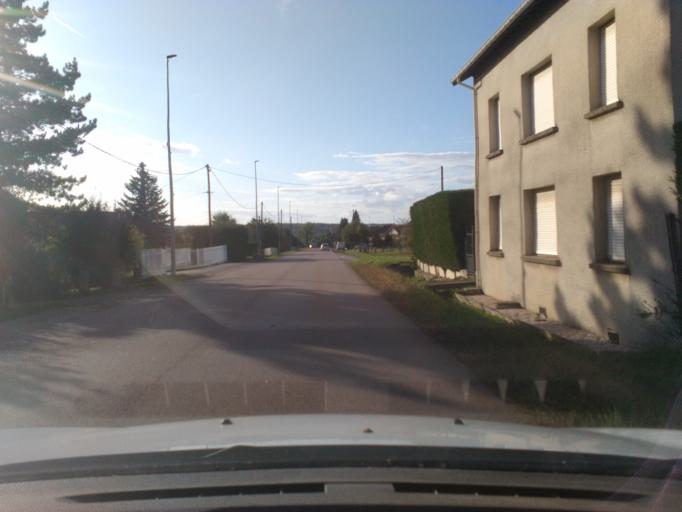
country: FR
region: Lorraine
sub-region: Departement des Vosges
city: Rambervillers
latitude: 48.3419
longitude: 6.6485
